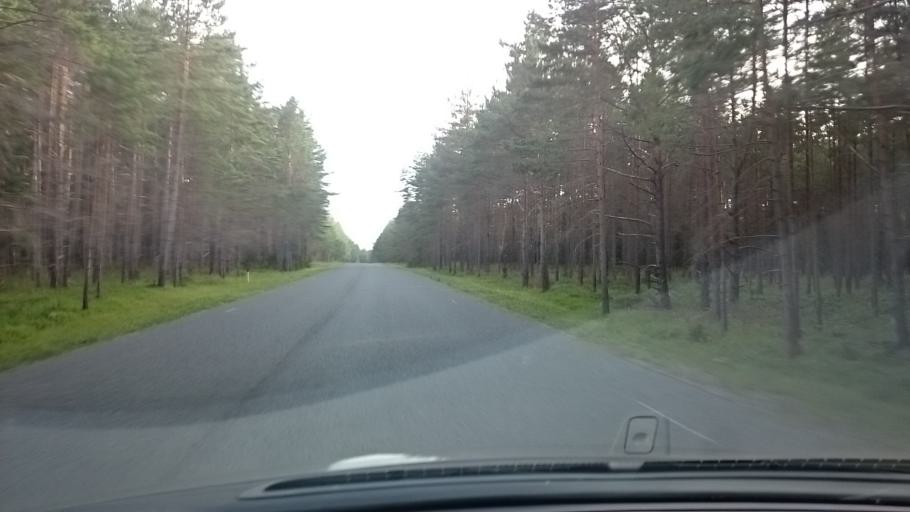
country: EE
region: Saare
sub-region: Kuressaare linn
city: Kuressaare
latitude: 58.4260
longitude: 22.1810
